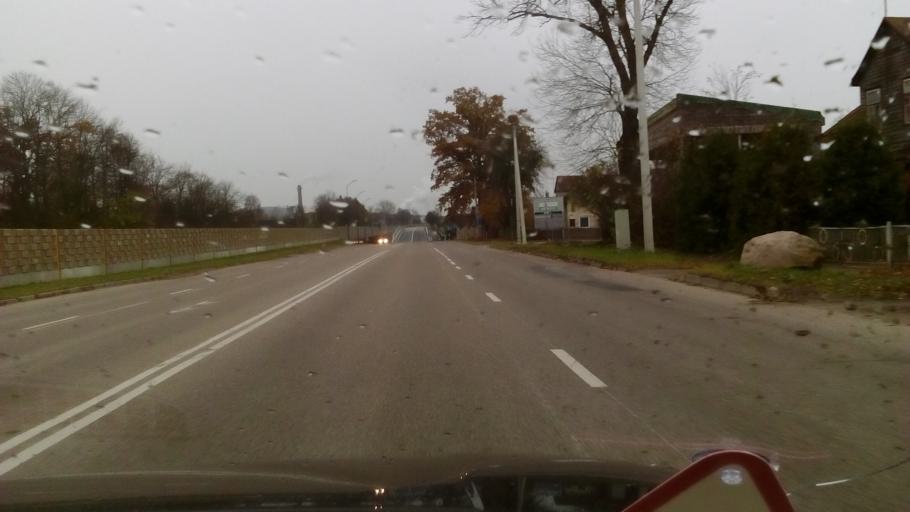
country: LT
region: Marijampoles apskritis
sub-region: Marijampole Municipality
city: Marijampole
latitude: 54.5469
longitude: 23.3573
